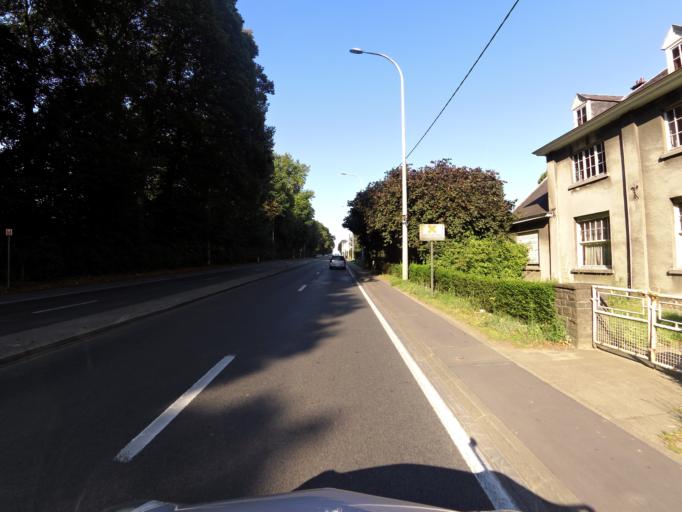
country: BE
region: Flanders
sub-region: Provincie Vlaams-Brabant
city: Dilbeek
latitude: 50.8428
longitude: 4.2499
